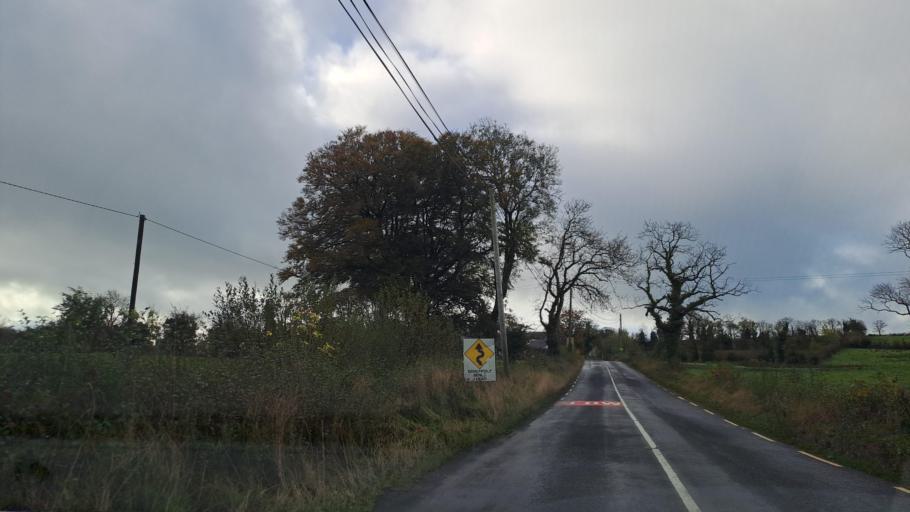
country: IE
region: Ulster
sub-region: An Cabhan
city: Virginia
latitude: 53.8607
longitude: -7.0456
